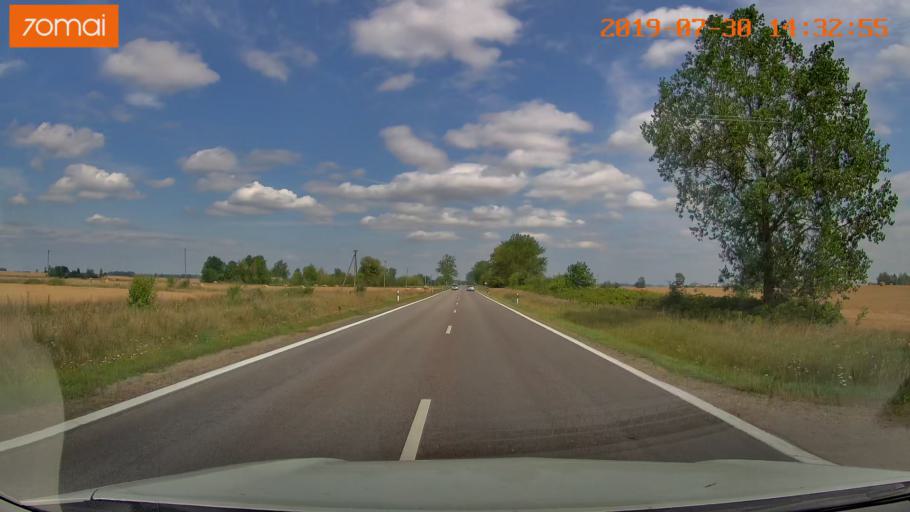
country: LT
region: Marijampoles apskritis
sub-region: Marijampole Municipality
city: Marijampole
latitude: 54.5544
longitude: 23.5053
